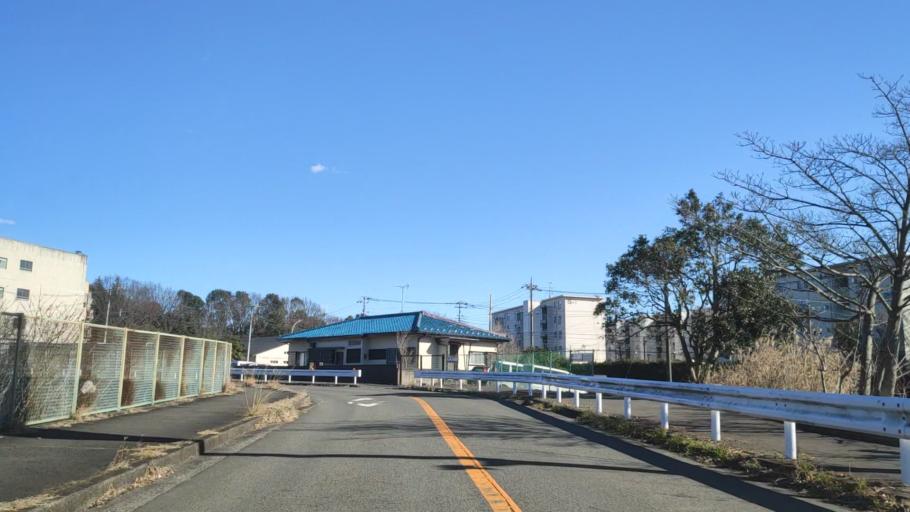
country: JP
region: Kanagawa
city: Minami-rinkan
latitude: 35.5032
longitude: 139.5291
